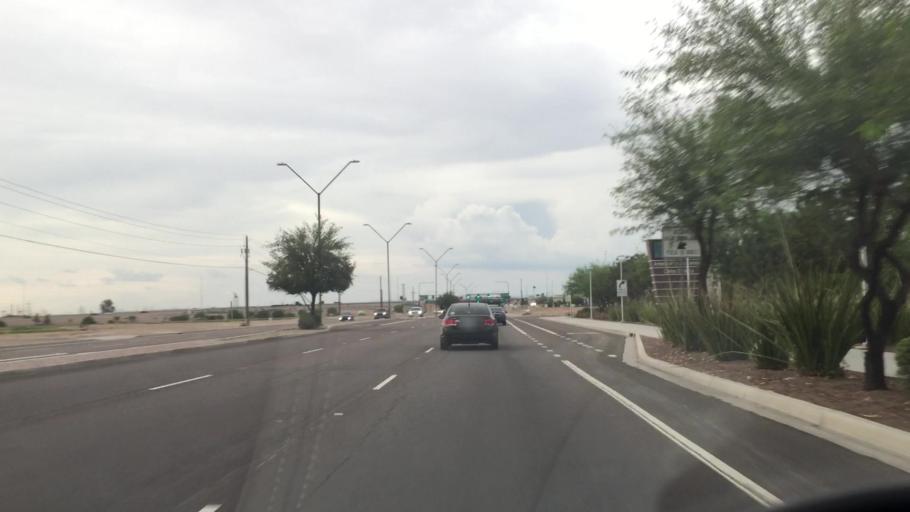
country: US
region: Arizona
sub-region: Maricopa County
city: Tolleson
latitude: 33.4549
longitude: -112.3062
